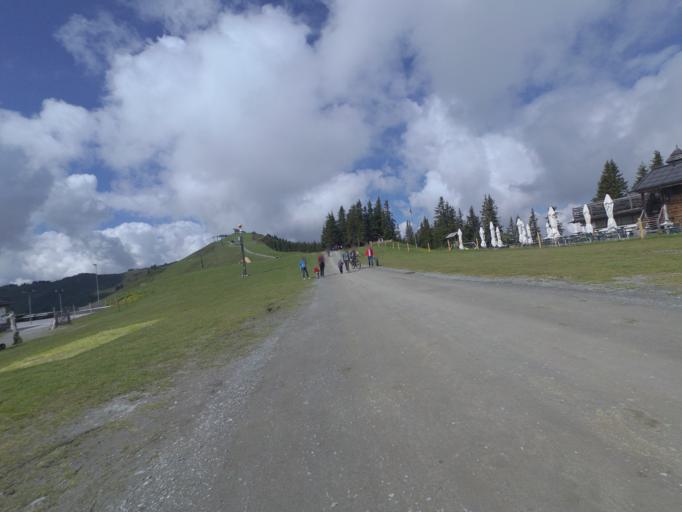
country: AT
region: Salzburg
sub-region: Politischer Bezirk Zell am See
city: Viehhofen
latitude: 47.4104
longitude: 12.7140
